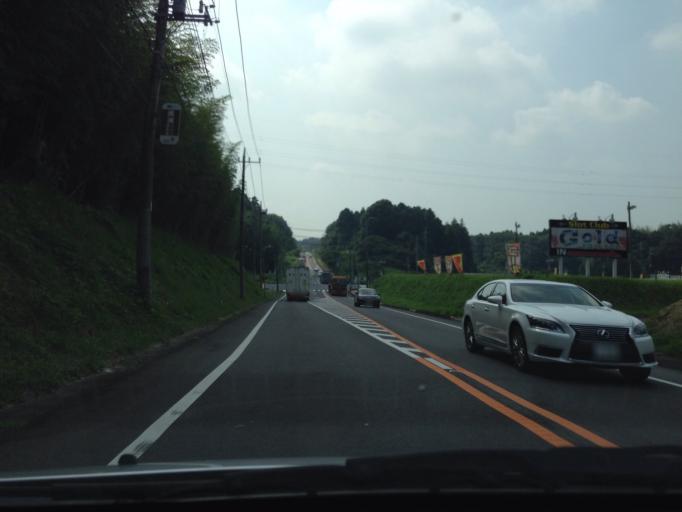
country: JP
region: Ibaraki
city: Inashiki
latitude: 36.0140
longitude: 140.2890
